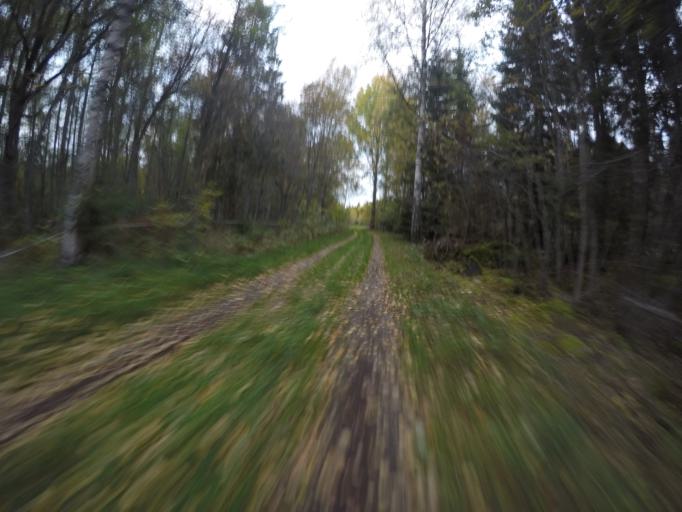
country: SE
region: Vaestmanland
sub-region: Arboga Kommun
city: Tyringe
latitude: 59.3314
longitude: 15.9686
